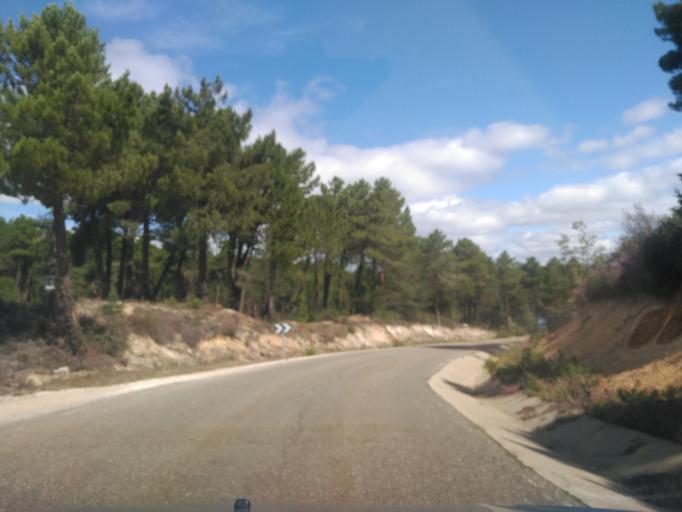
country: ES
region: Castille and Leon
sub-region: Provincia de Soria
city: Espejon
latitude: 41.8439
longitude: -3.2379
